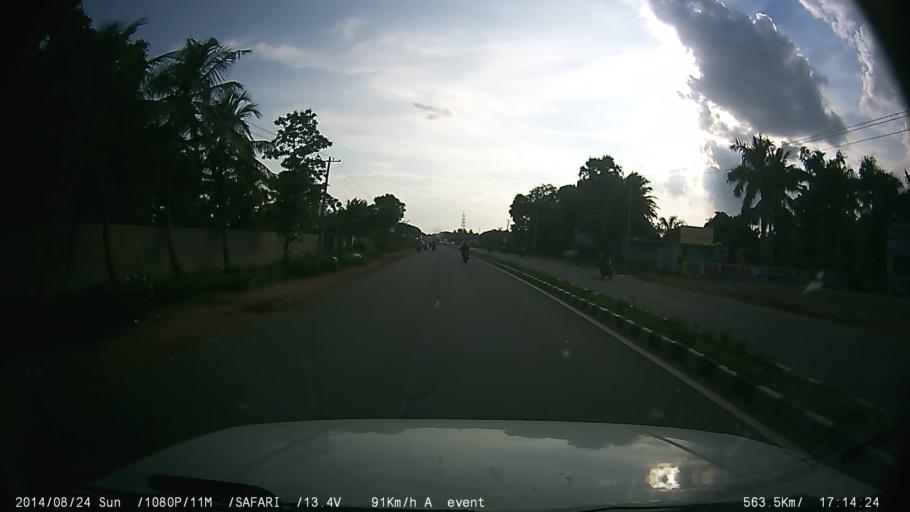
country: IN
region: Tamil Nadu
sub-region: Kancheepuram
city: Vandalur
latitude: 12.8944
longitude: 80.0471
